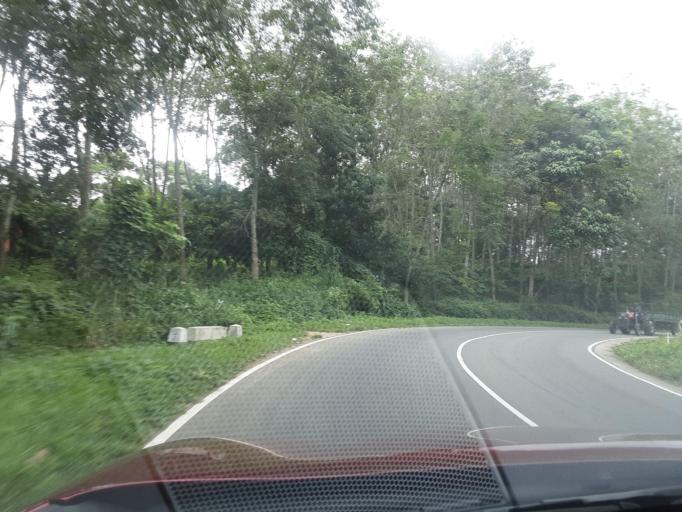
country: LK
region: Uva
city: Monaragala
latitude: 6.9019
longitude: 81.2171
